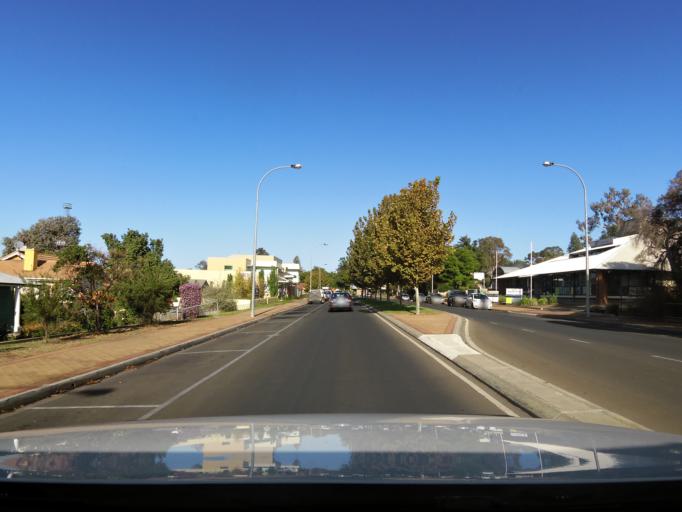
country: AU
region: South Australia
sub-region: Berri and Barmera
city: Berri
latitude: -34.2840
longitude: 140.6038
